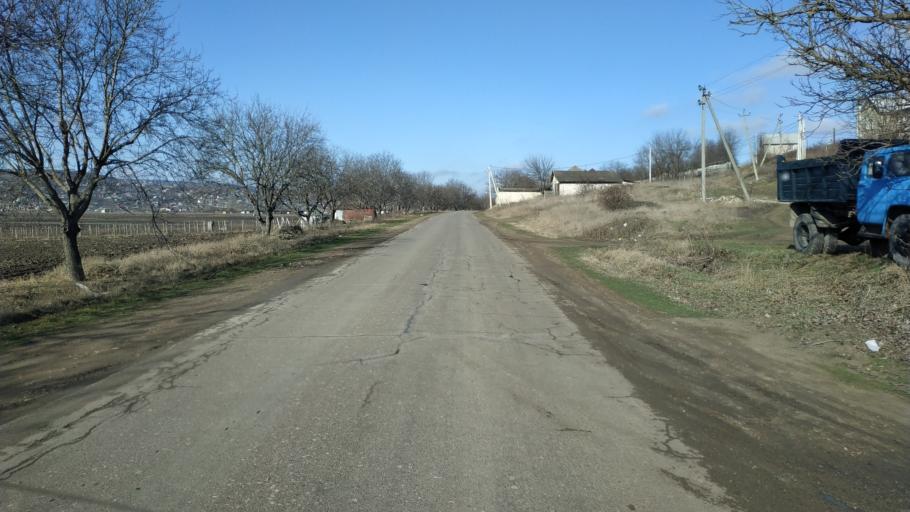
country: MD
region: Laloveni
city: Ialoveni
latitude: 46.9306
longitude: 28.6686
